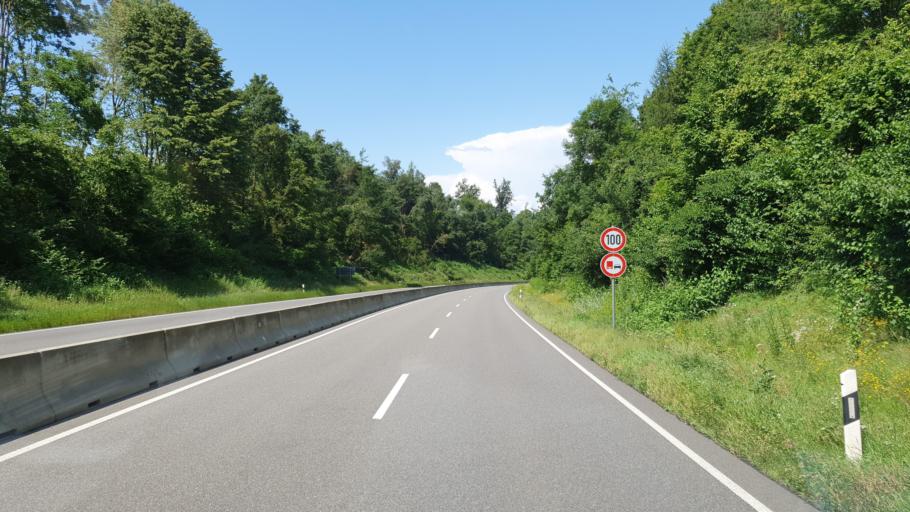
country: DE
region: Baden-Wuerttemberg
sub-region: Tuebingen Region
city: Uhldingen-Muhlhofen
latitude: 47.7206
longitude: 9.2417
